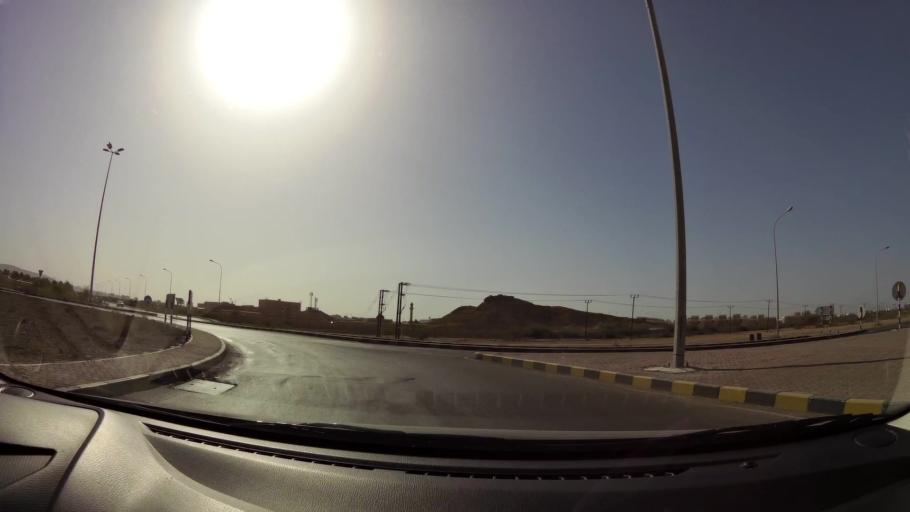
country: OM
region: Muhafazat Masqat
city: As Sib al Jadidah
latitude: 23.5765
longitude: 58.2119
